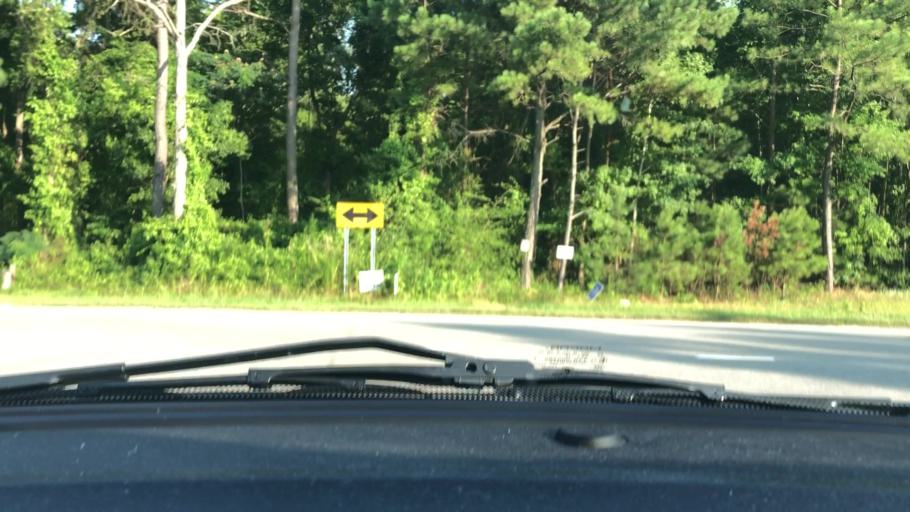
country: US
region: North Carolina
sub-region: Lee County
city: Broadway
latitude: 35.3238
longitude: -79.0705
